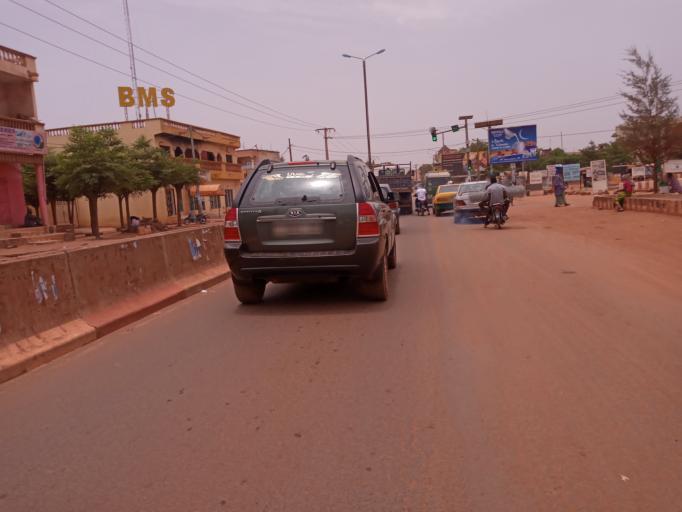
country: ML
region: Bamako
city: Bamako
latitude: 12.5842
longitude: -8.0230
